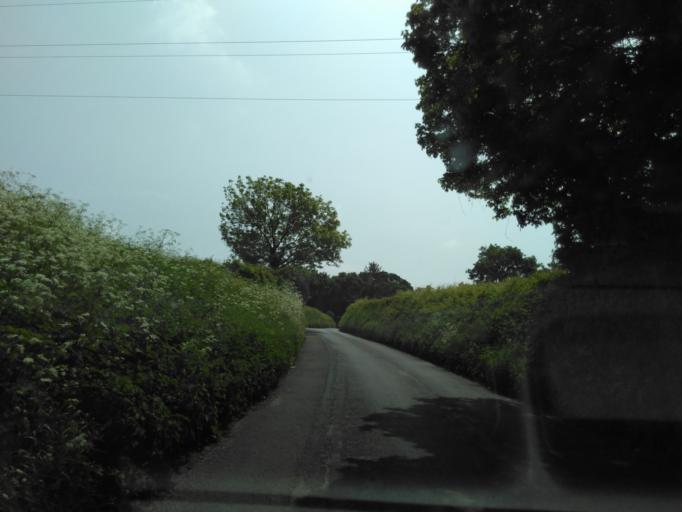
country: GB
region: England
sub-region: Kent
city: Chartham
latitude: 51.2515
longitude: 1.0235
